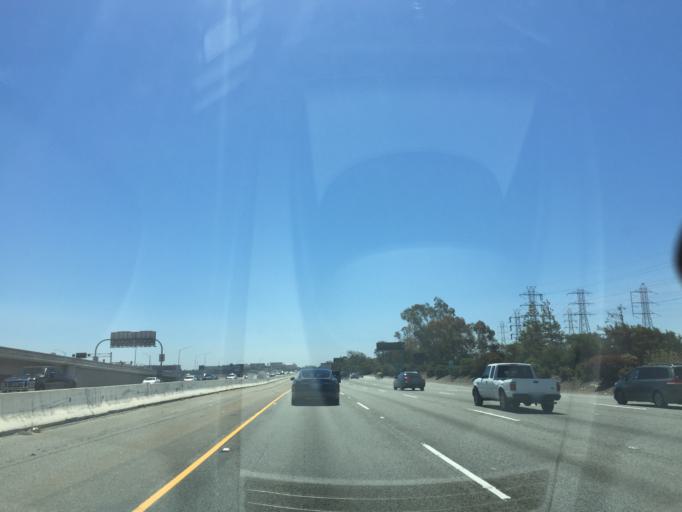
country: US
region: California
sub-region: San Mateo County
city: Millbrae
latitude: 37.6088
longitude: -122.3900
